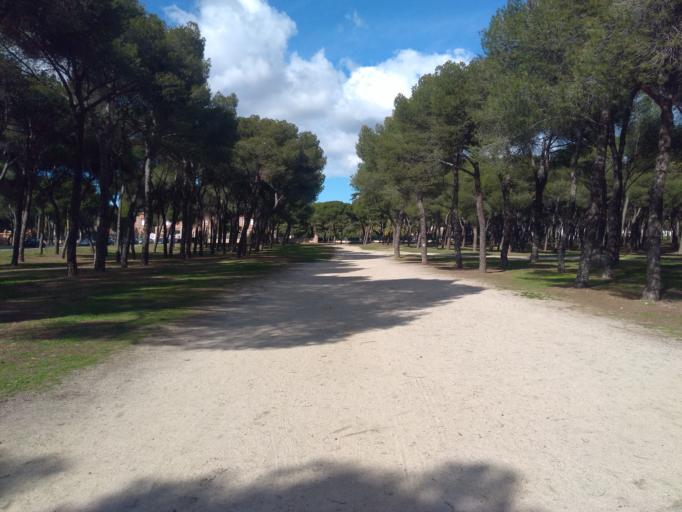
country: ES
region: Madrid
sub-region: Provincia de Madrid
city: Leganes
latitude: 40.3616
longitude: -3.7712
